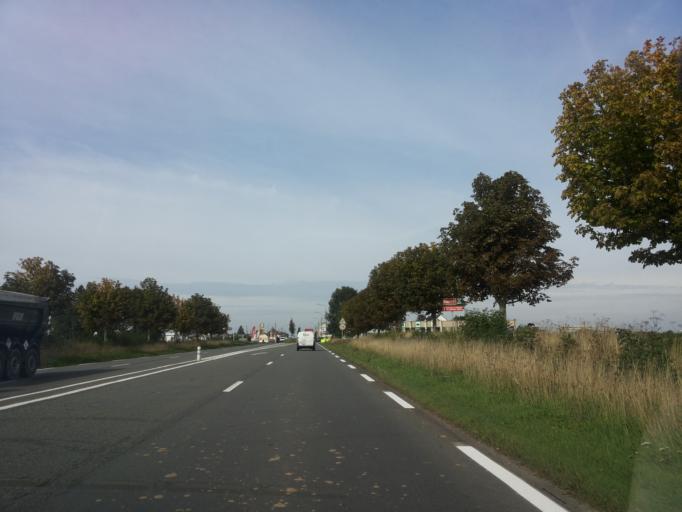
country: FR
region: Nord-Pas-de-Calais
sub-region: Departement du Pas-de-Calais
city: Tilloy-les-Mofflaines
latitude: 50.2773
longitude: 2.8254
